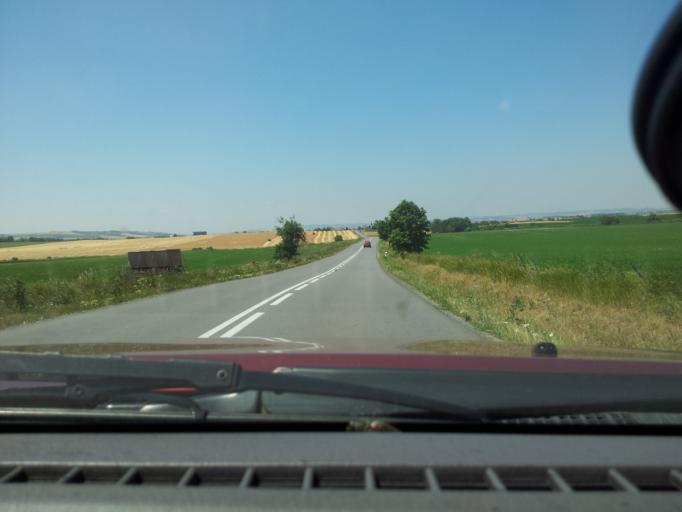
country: CZ
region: South Moravian
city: Tesany
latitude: 49.0430
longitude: 16.7581
